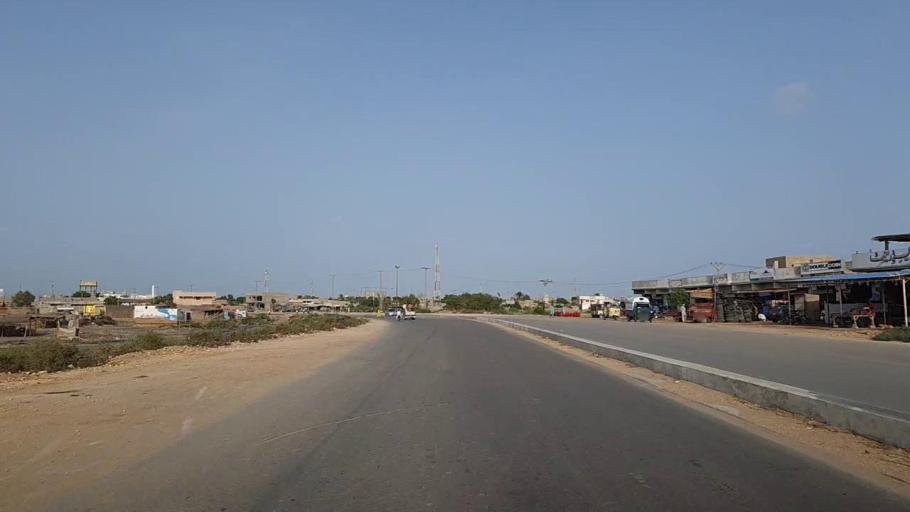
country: PK
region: Sindh
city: Thatta
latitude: 24.7487
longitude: 67.9128
